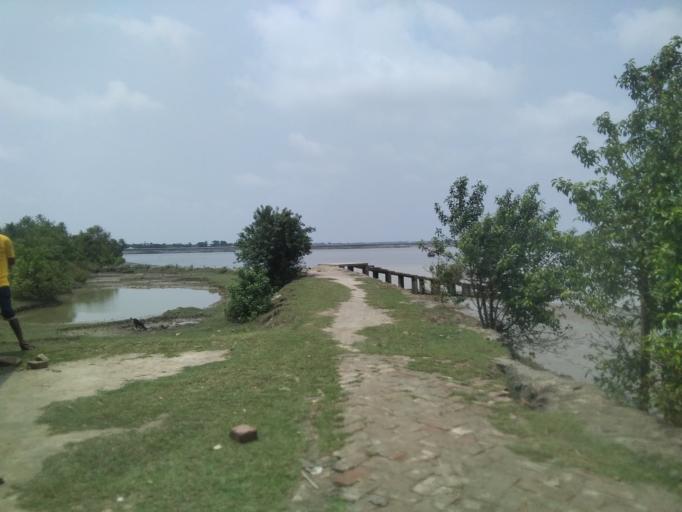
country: BD
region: Khulna
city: Phultala
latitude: 22.6409
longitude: 89.4140
